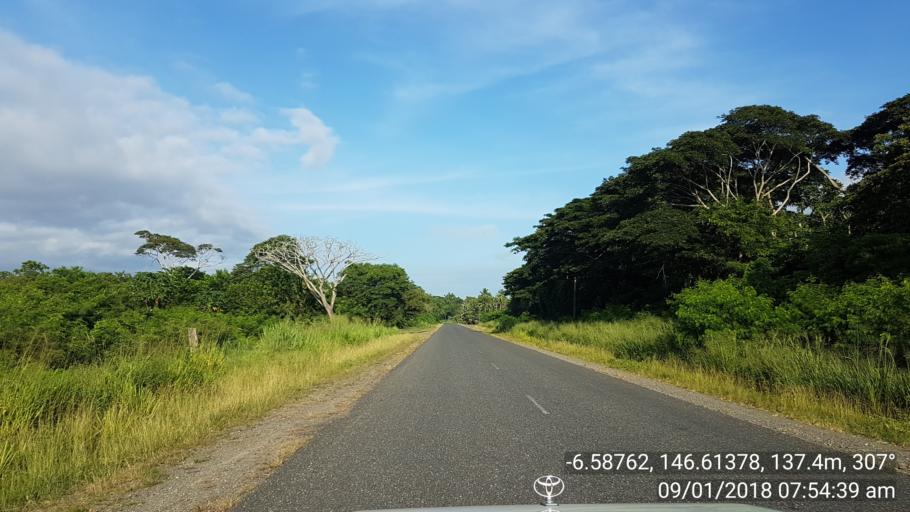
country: PG
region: Morobe
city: Lae
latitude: -6.5878
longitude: 146.6140
